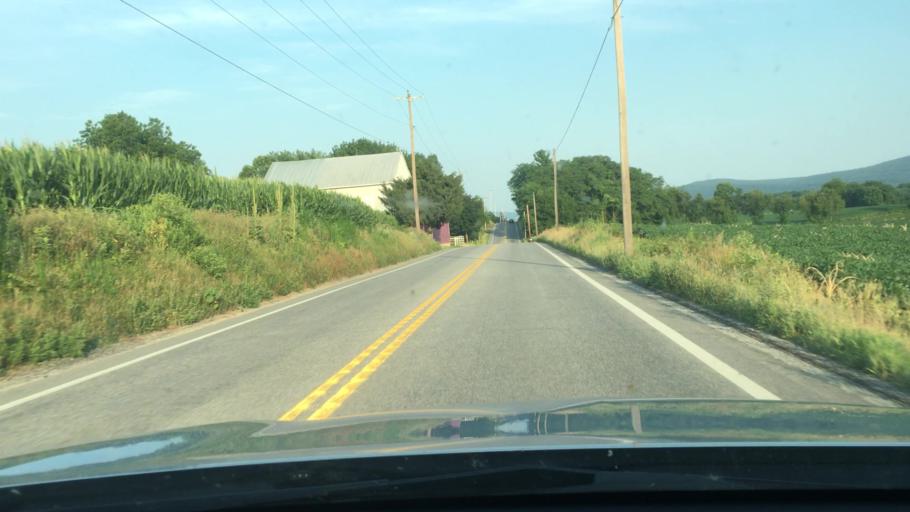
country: US
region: Pennsylvania
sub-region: Cumberland County
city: Boiling Springs
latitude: 40.1671
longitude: -77.1086
